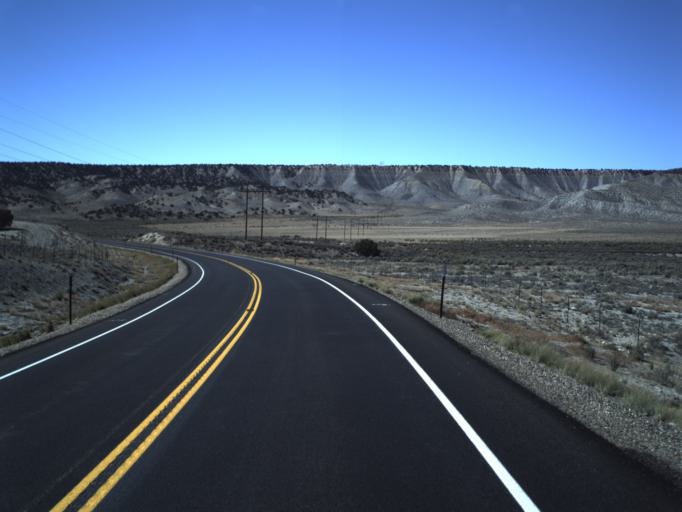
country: US
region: Utah
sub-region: Garfield County
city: Panguitch
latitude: 37.6026
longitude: -111.9617
